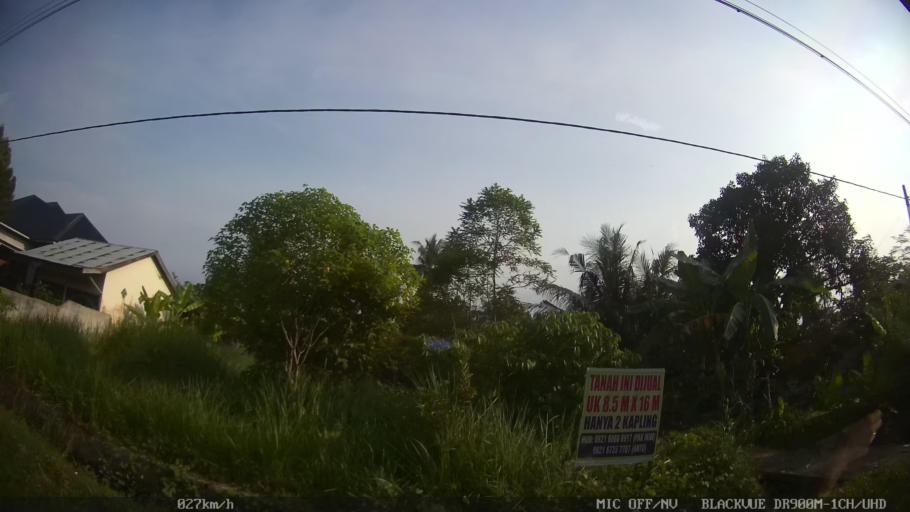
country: ID
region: North Sumatra
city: Binjai
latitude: 3.6210
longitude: 98.5299
